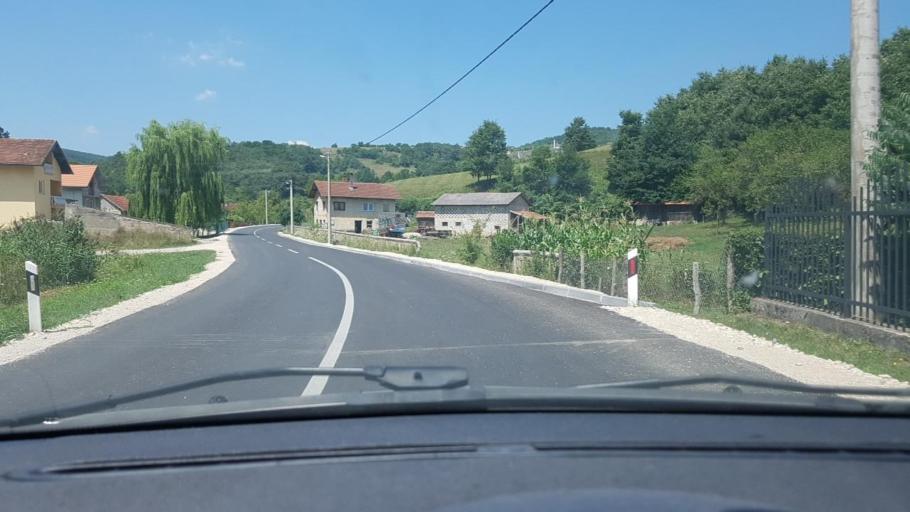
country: BA
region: Federation of Bosnia and Herzegovina
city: Orasac
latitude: 44.6186
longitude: 16.0713
